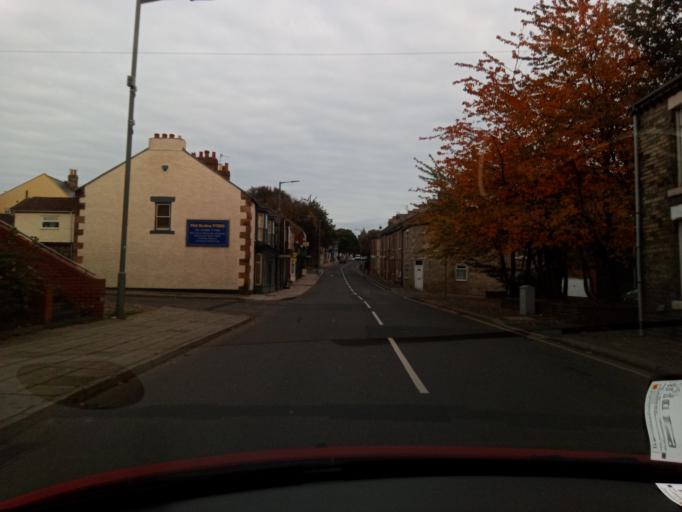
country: GB
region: England
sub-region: County Durham
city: Shildon
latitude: 54.6325
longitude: -1.6525
